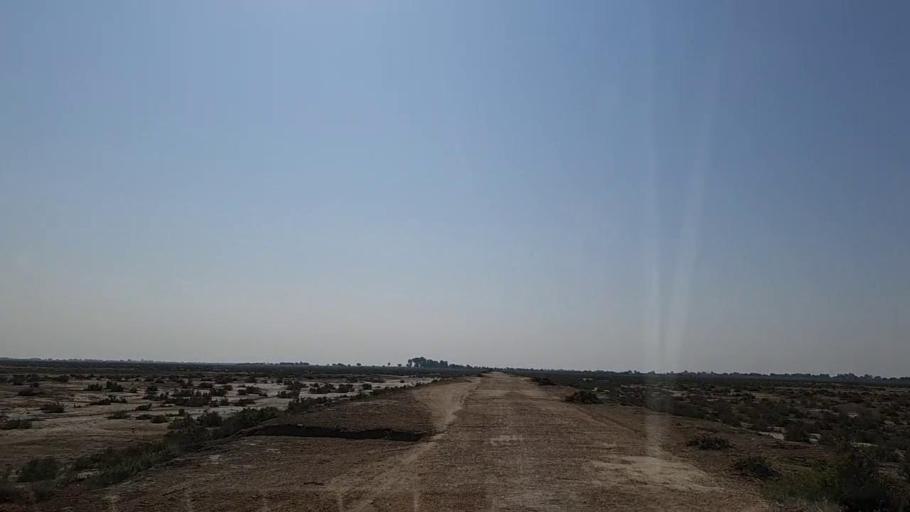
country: PK
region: Sindh
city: Chuhar Jamali
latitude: 24.5086
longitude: 68.0978
